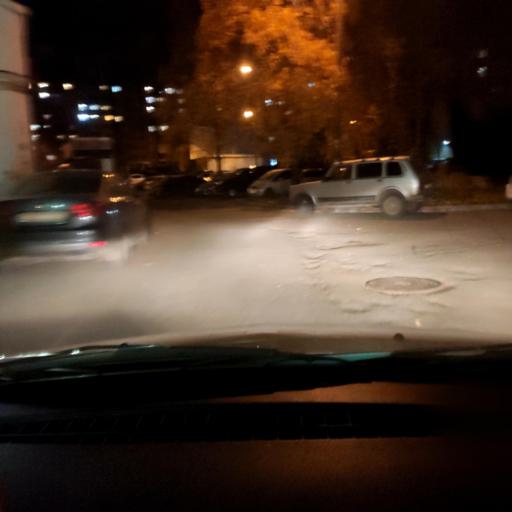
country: RU
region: Bashkortostan
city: Ufa
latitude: 54.6995
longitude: 55.9984
